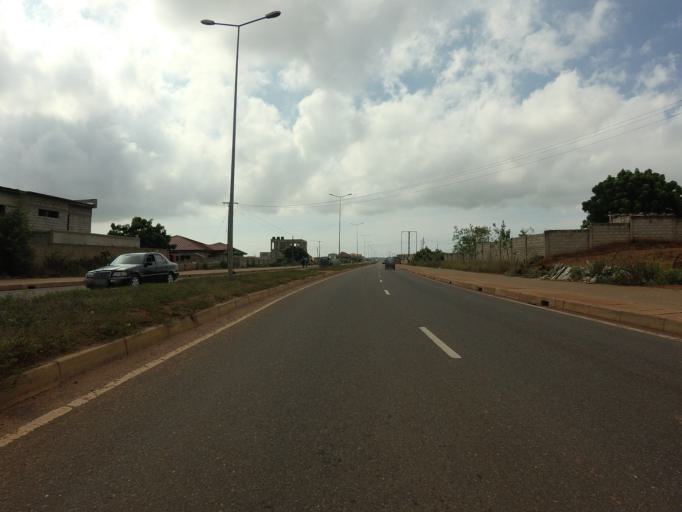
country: GH
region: Greater Accra
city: Teshi Old Town
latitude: 5.6059
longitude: -0.1392
